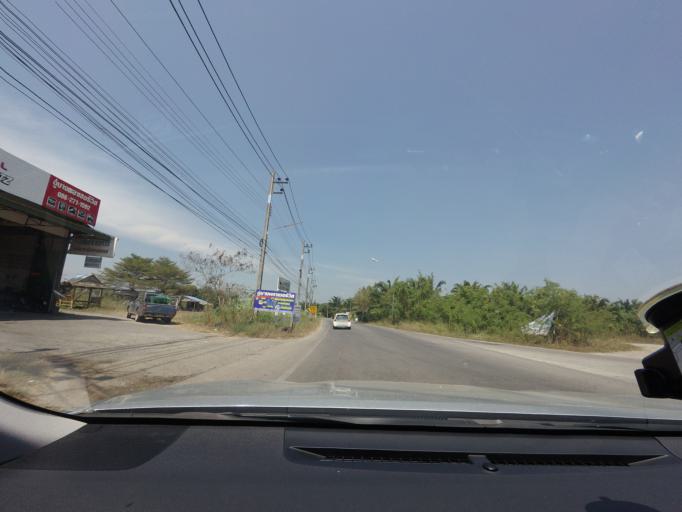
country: TH
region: Surat Thani
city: Phunphin
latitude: 9.1915
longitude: 99.2578
